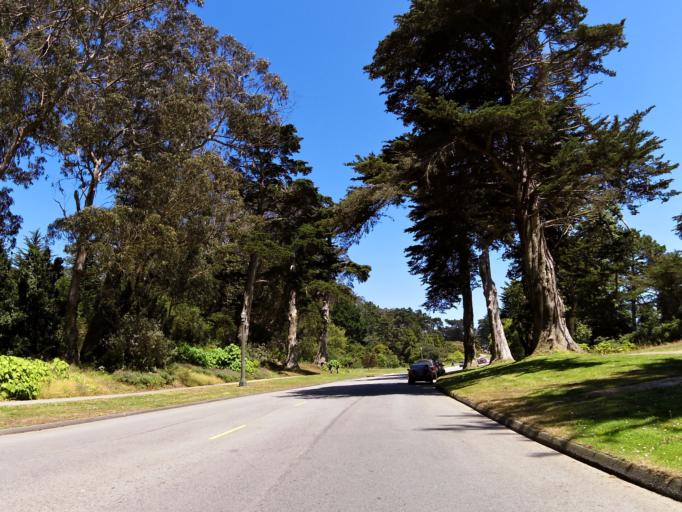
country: US
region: California
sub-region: San Francisco County
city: San Francisco
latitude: 37.7667
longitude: -122.4814
